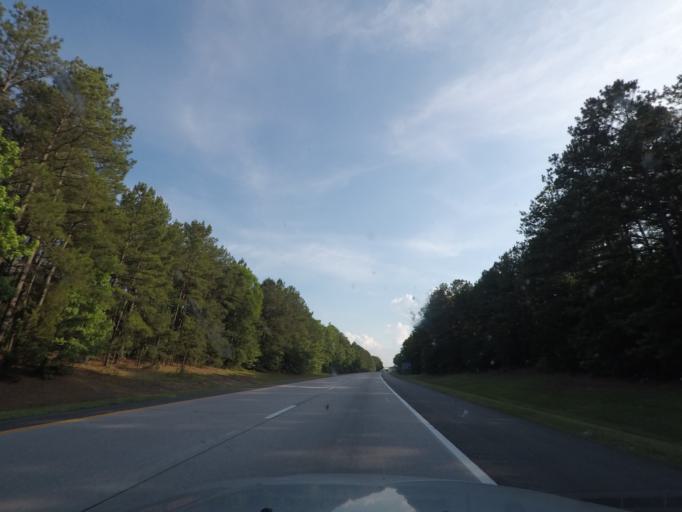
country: US
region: North Carolina
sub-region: Granville County
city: Creedmoor
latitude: 36.1592
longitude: -78.7150
